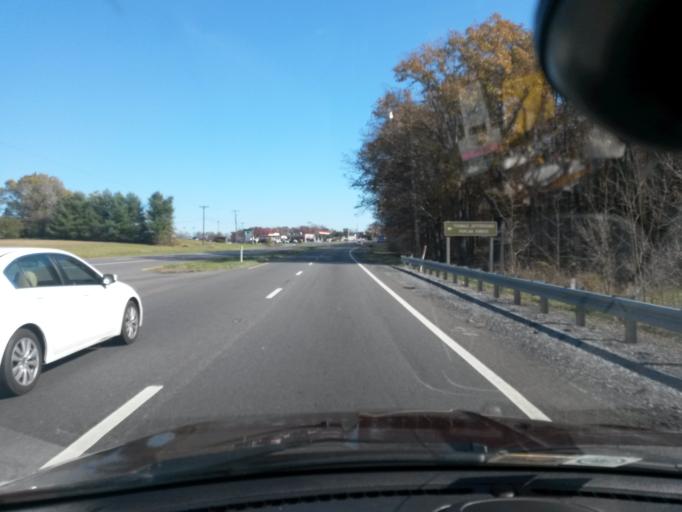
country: US
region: Virginia
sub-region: Campbell County
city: Timberlake
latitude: 37.3056
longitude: -79.3124
